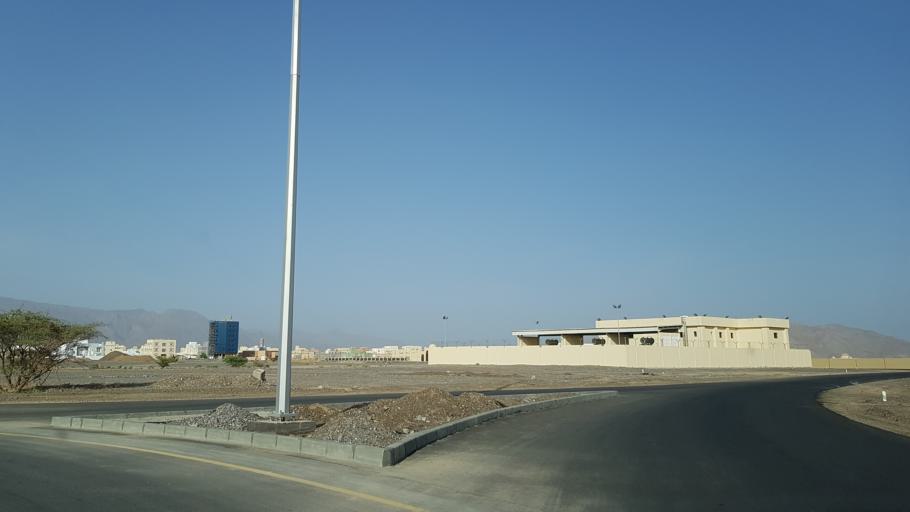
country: OM
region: Muhafazat ad Dakhiliyah
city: Nizwa
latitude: 22.8673
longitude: 57.5385
